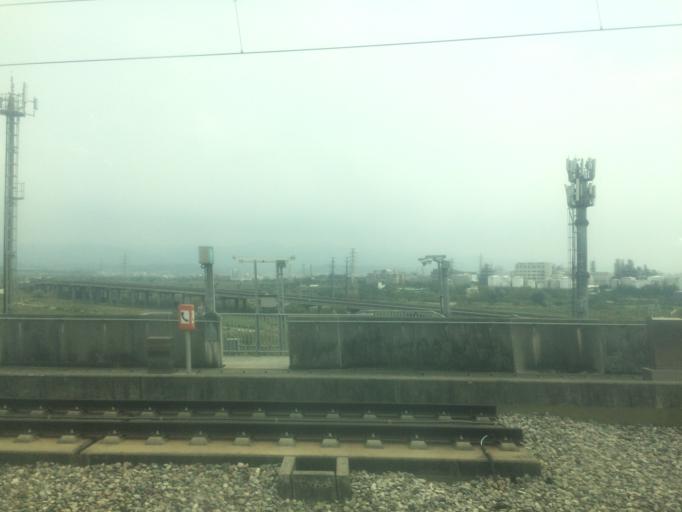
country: TW
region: Taiwan
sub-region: Miaoli
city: Miaoli
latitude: 24.6025
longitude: 120.8185
